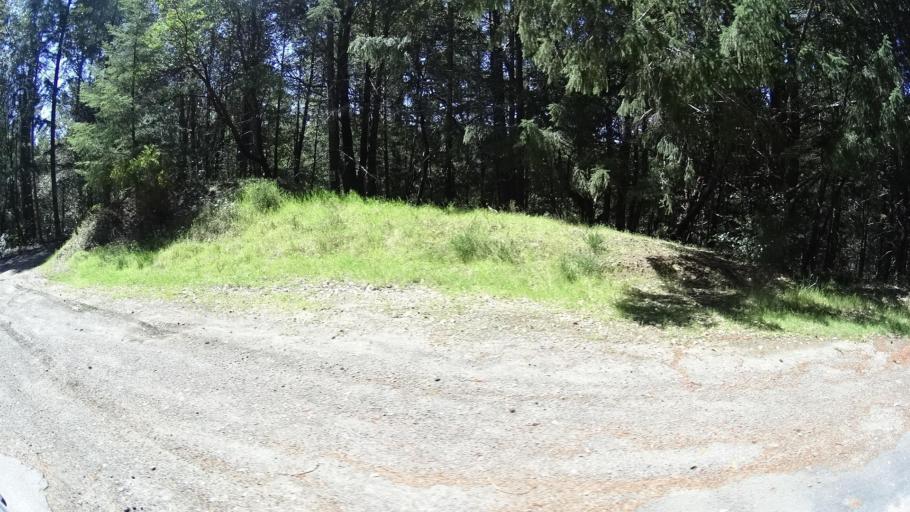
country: US
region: California
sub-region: Humboldt County
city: Redway
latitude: 40.1026
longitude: -123.9520
